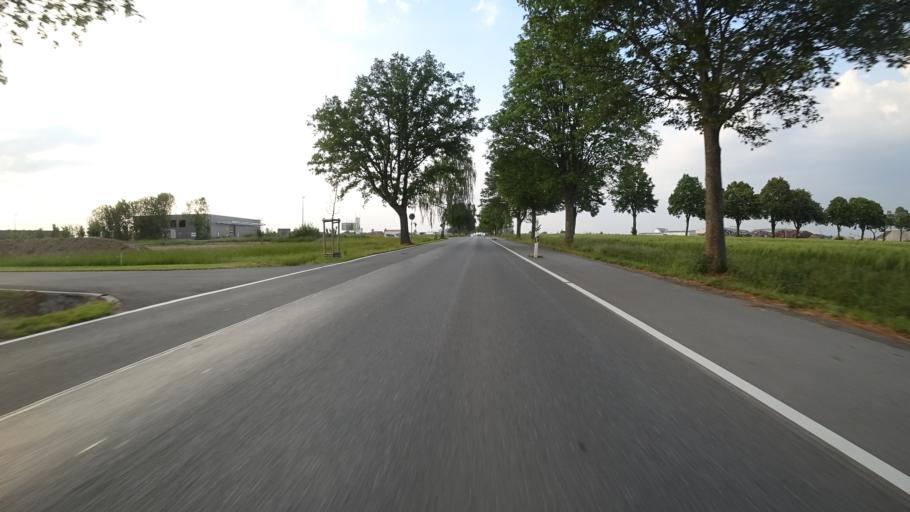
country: DE
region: North Rhine-Westphalia
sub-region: Regierungsbezirk Arnsberg
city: Lippstadt
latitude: 51.6465
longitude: 8.3577
